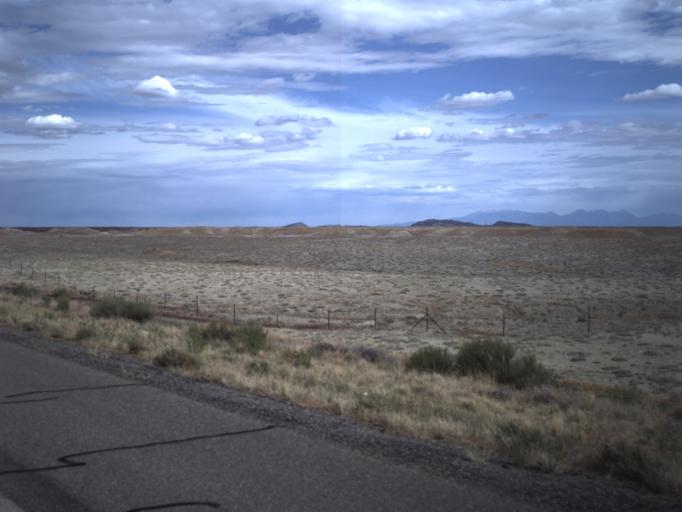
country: US
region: Utah
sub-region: Grand County
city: Moab
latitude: 38.9247
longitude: -109.9110
